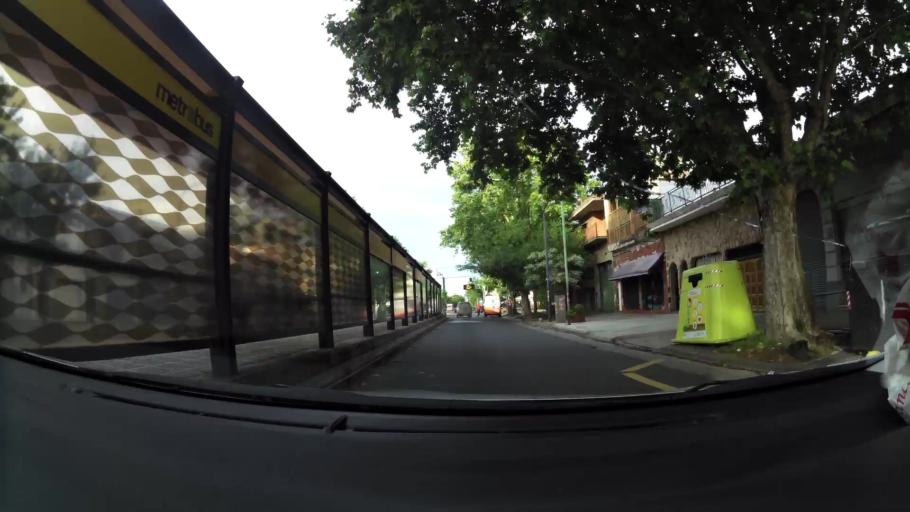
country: AR
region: Buenos Aires F.D.
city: Buenos Aires
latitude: -34.6439
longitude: -58.4241
